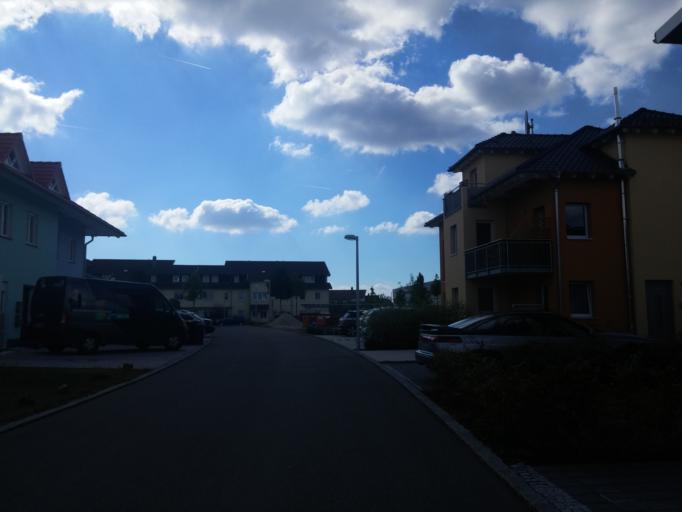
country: DE
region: Bavaria
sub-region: Upper Franconia
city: Coburg
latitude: 50.2783
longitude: 10.9694
